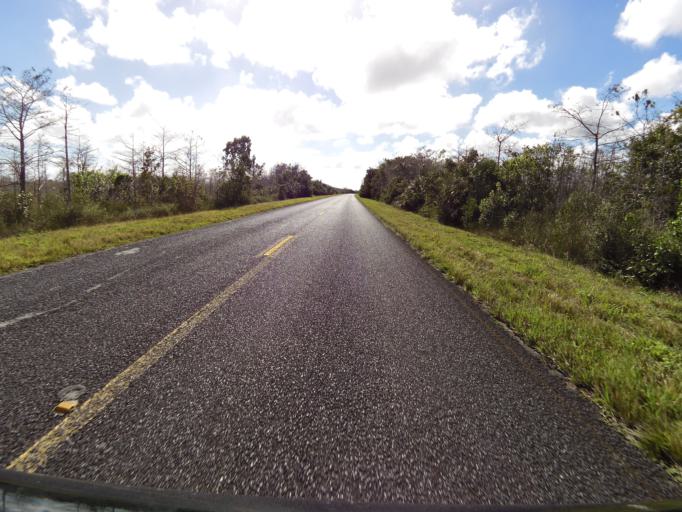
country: US
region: Florida
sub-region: Miami-Dade County
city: Florida City
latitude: 25.4166
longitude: -80.7802
